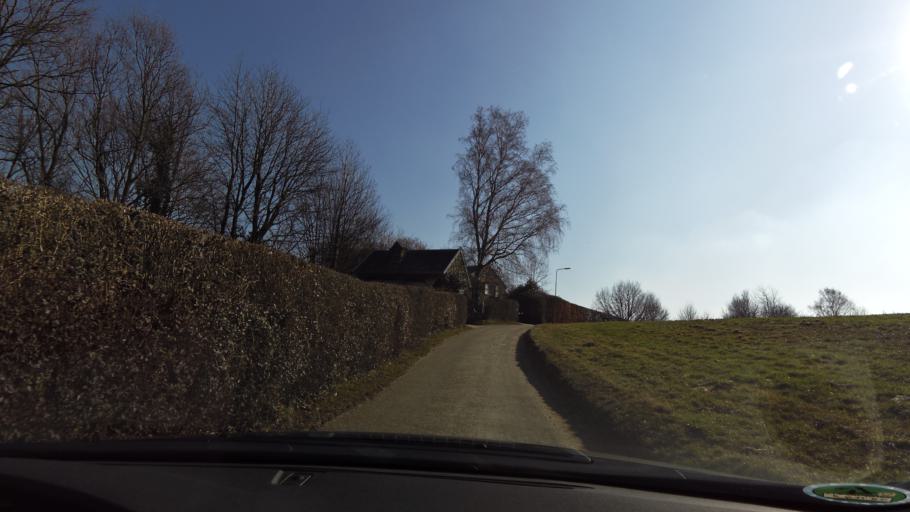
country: BE
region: Wallonia
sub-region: Province de Liege
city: Plombieres
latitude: 50.7767
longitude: 5.8984
